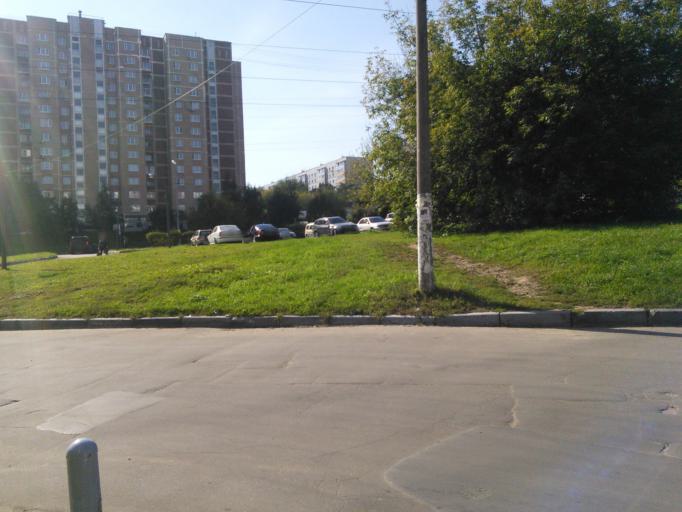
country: RU
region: Moscow
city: Orekhovo-Borisovo Severnoye
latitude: 55.6375
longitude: 37.6784
